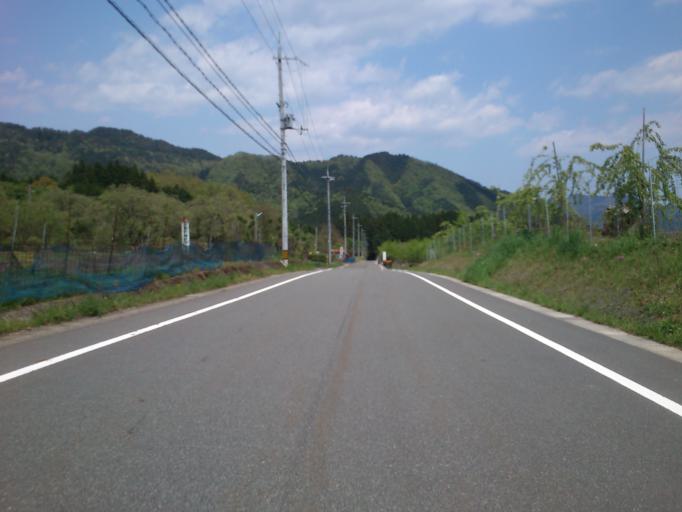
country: JP
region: Kyoto
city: Fukuchiyama
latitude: 35.3386
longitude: 134.9214
